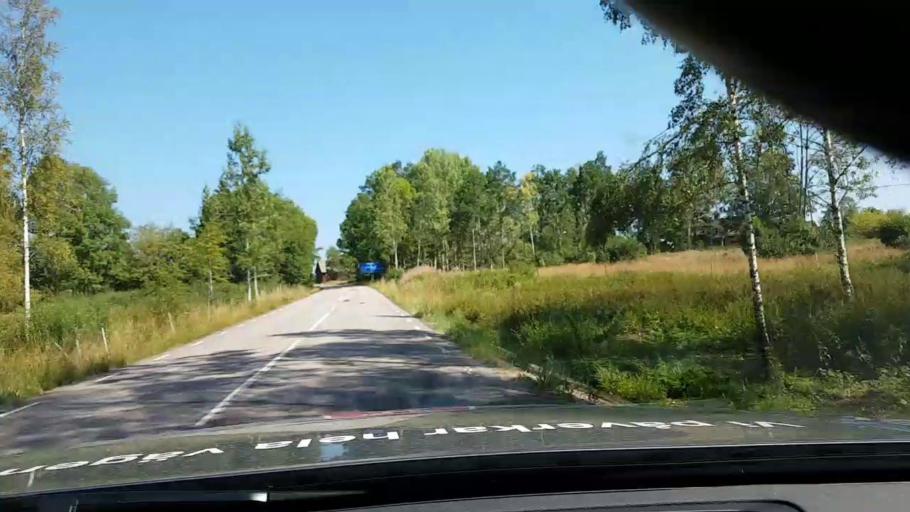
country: SE
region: Kalmar
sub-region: Hultsfreds Kommun
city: Virserum
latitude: 57.1333
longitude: 15.6589
